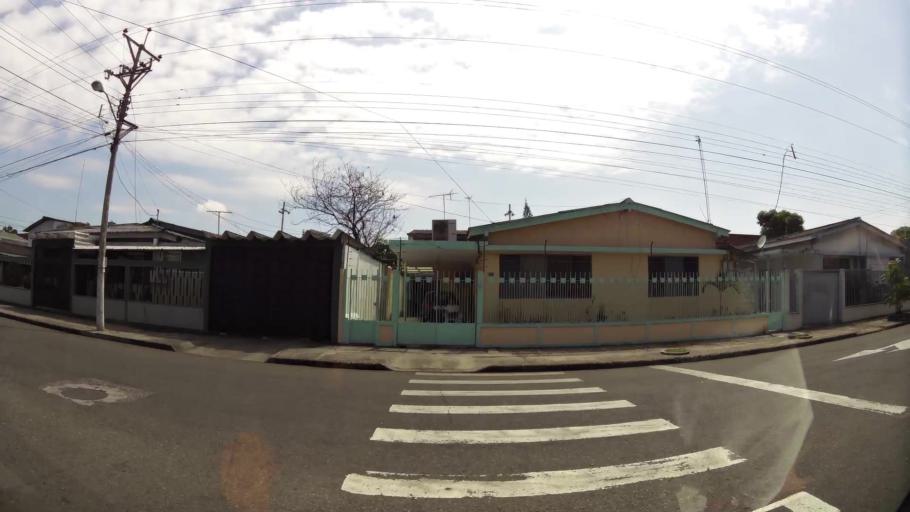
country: EC
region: Guayas
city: Guayaquil
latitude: -2.2316
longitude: -79.8947
